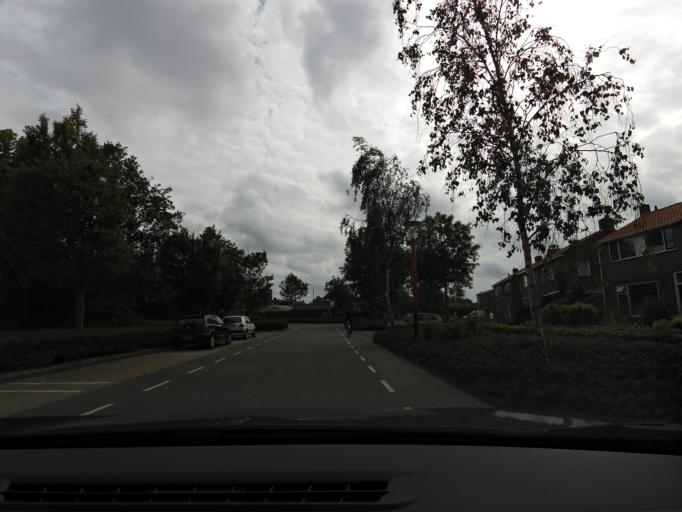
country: NL
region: Zeeland
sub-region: Gemeente Middelburg
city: Middelburg
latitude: 51.5696
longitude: 3.5525
